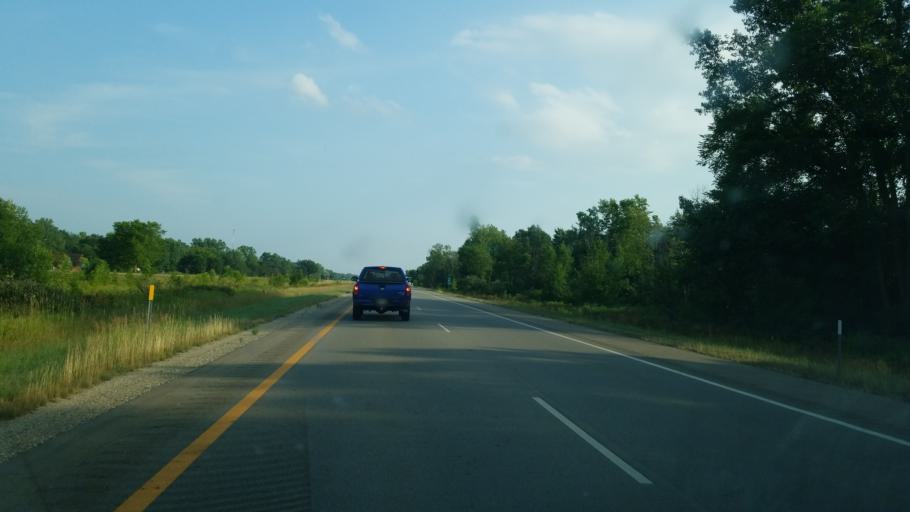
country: US
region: Michigan
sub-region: Gratiot County
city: Saint Louis
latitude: 43.3556
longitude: -84.6018
